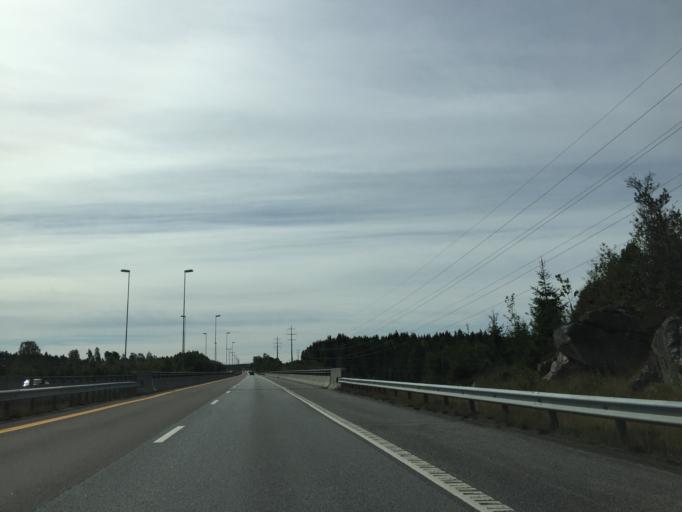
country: NO
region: Akershus
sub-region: Vestby
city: Vestby
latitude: 59.5577
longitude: 10.7212
